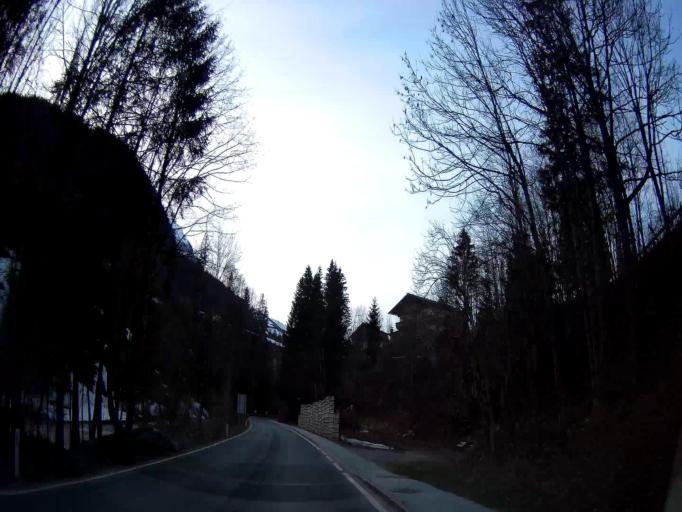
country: AT
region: Salzburg
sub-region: Politischer Bezirk Hallein
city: Abtenau
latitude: 47.5263
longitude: 13.4277
